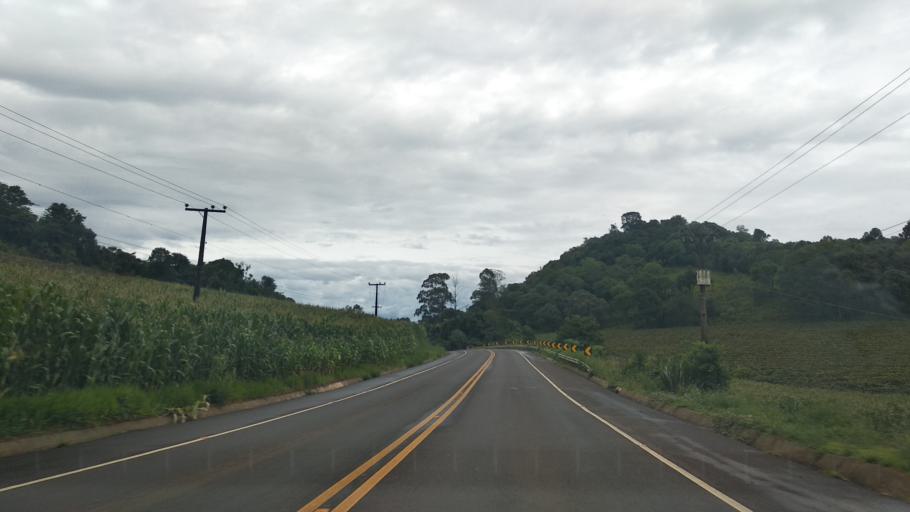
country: BR
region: Santa Catarina
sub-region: Videira
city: Videira
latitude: -27.0472
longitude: -51.1618
